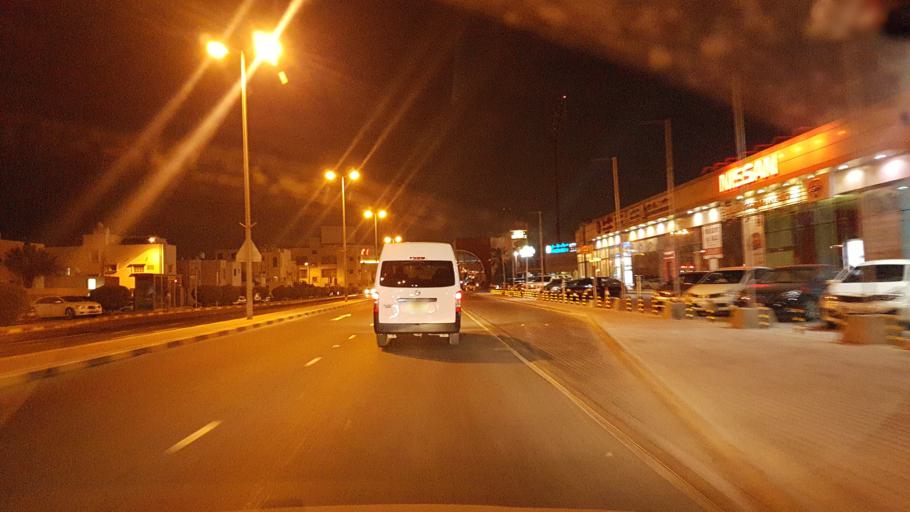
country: BH
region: Muharraq
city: Al Muharraq
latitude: 26.2584
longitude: 50.6293
